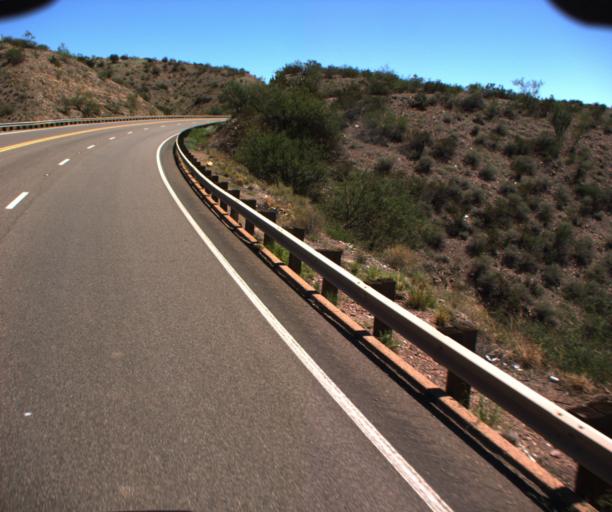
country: US
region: Arizona
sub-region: Greenlee County
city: Clifton
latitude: 33.0188
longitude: -109.2883
